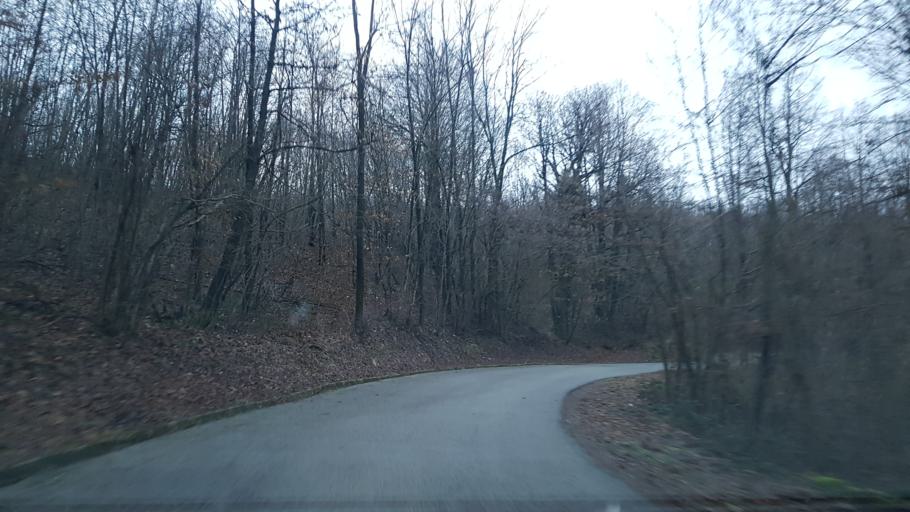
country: IT
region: Friuli Venezia Giulia
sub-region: Provincia di Udine
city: San Leonardo
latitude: 46.1019
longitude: 13.5576
